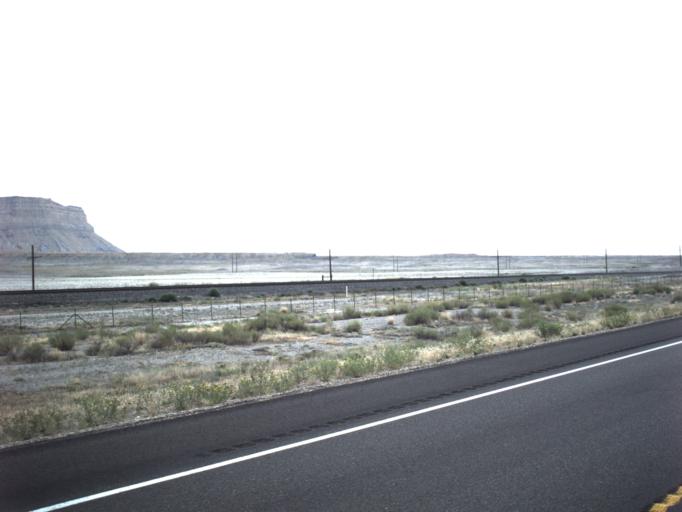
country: US
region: Utah
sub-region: Carbon County
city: East Carbon City
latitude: 39.0905
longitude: -110.3205
